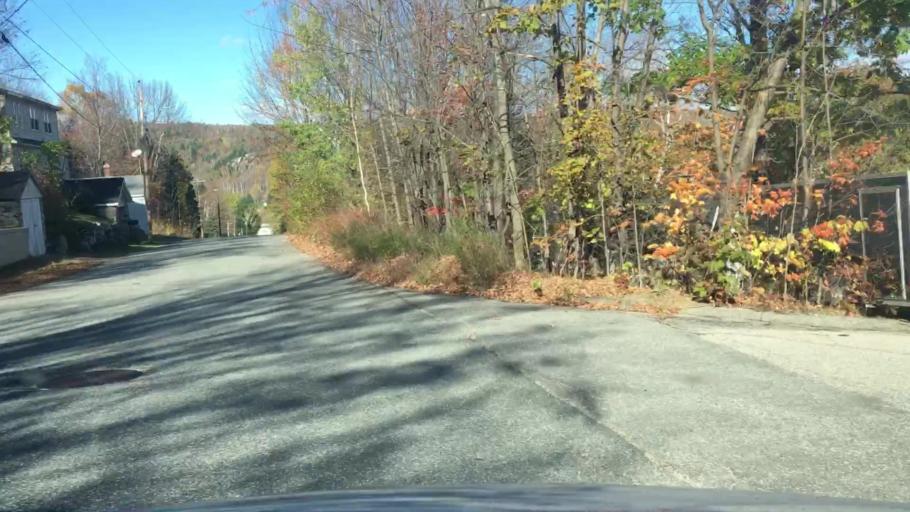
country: US
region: New Hampshire
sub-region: Coos County
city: Berlin
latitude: 44.4709
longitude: -71.1917
